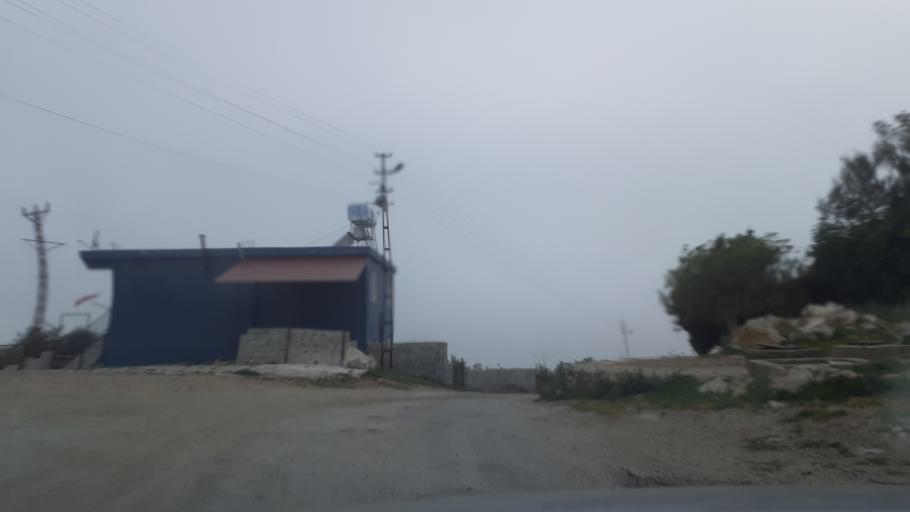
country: TR
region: Hatay
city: Yeditepe
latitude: 35.9690
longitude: 36.0059
